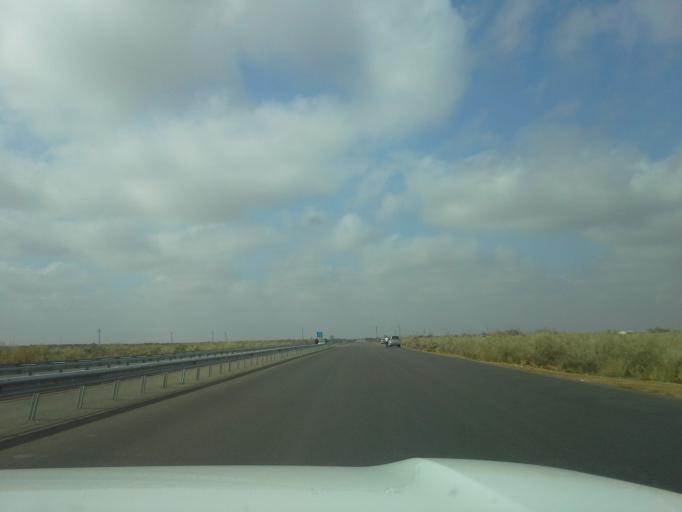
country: TM
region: Mary
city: Mary
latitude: 37.4208
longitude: 61.5739
